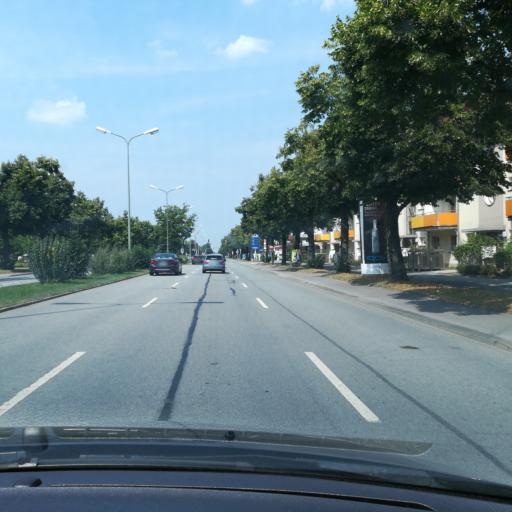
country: DE
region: Bavaria
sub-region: Upper Bavaria
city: Neuried
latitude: 48.1186
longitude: 11.5026
